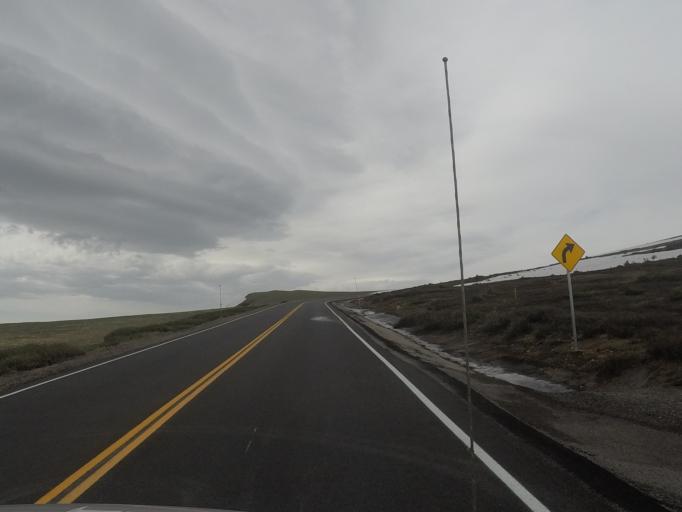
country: US
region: Montana
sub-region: Carbon County
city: Red Lodge
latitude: 45.0207
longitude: -109.4019
